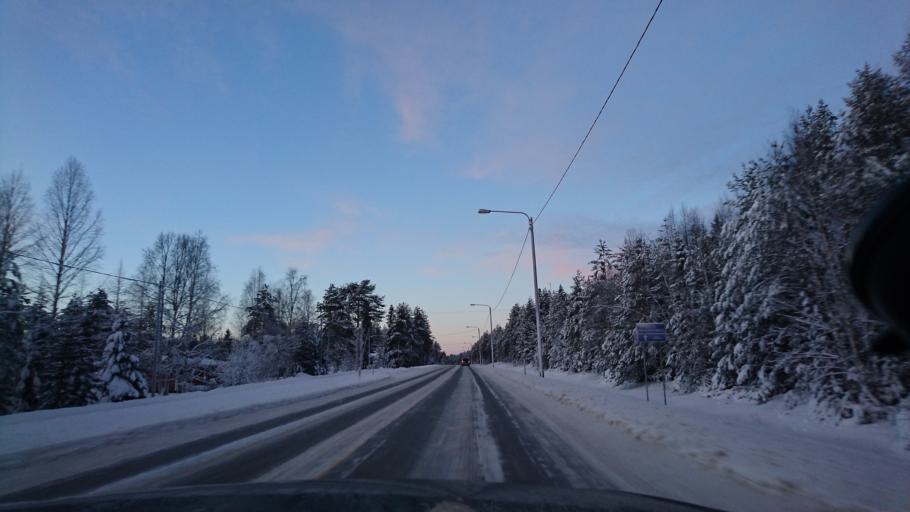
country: FI
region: Lapland
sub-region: Rovaniemi
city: Ranua
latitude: 65.9396
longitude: 26.4834
